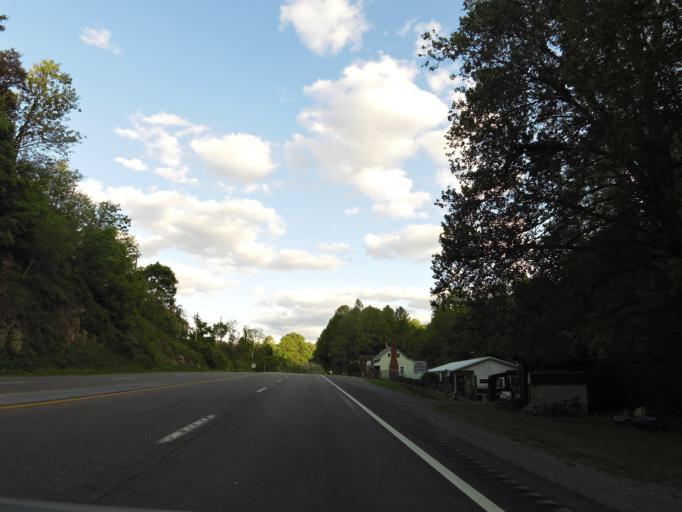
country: US
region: Virginia
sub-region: Washington County
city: Abingdon
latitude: 36.7383
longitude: -82.0394
